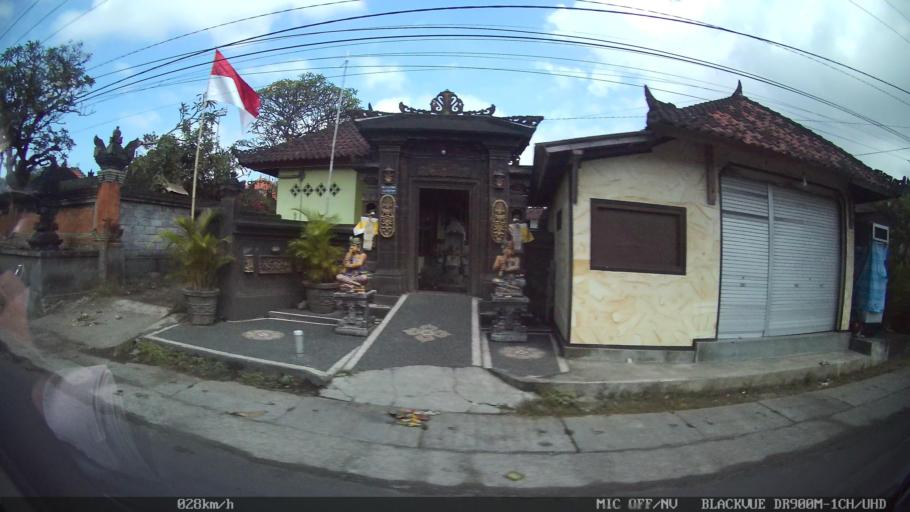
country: ID
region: Bali
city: Banjar Pasekan
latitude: -8.6031
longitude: 115.2922
